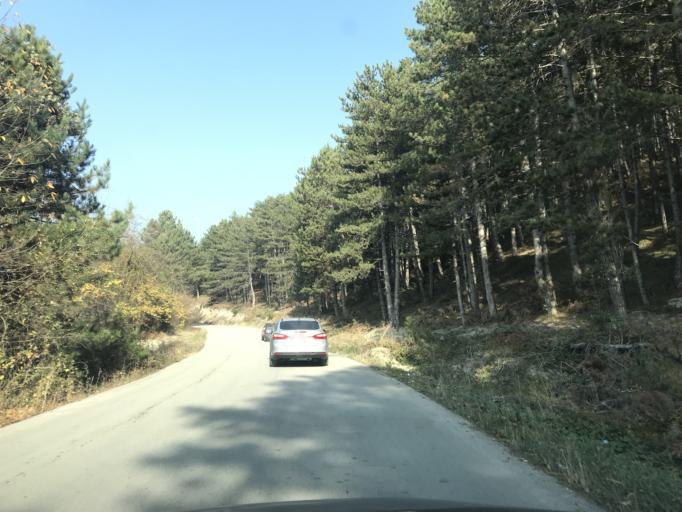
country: TR
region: Bolu
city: Bolu
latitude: 40.7812
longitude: 31.6327
